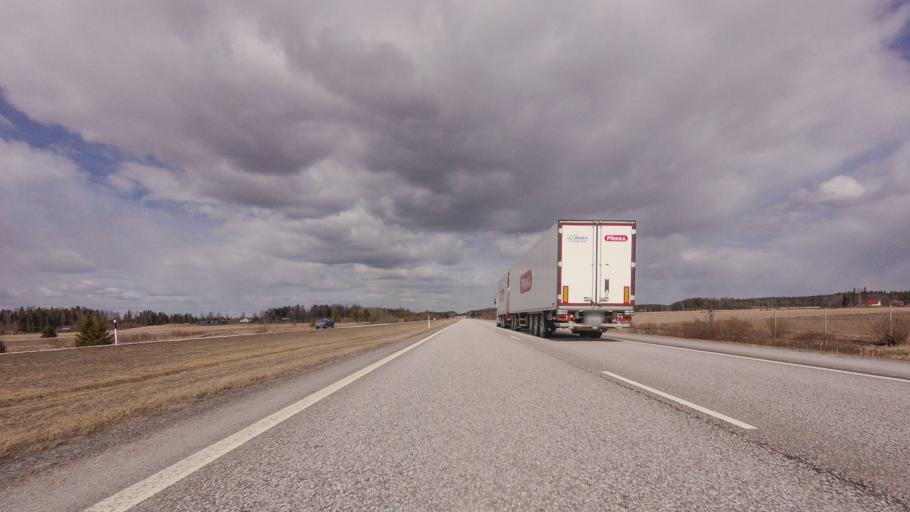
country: FI
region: Uusimaa
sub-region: Helsinki
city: Nurmijaervi
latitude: 60.5269
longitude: 24.8437
